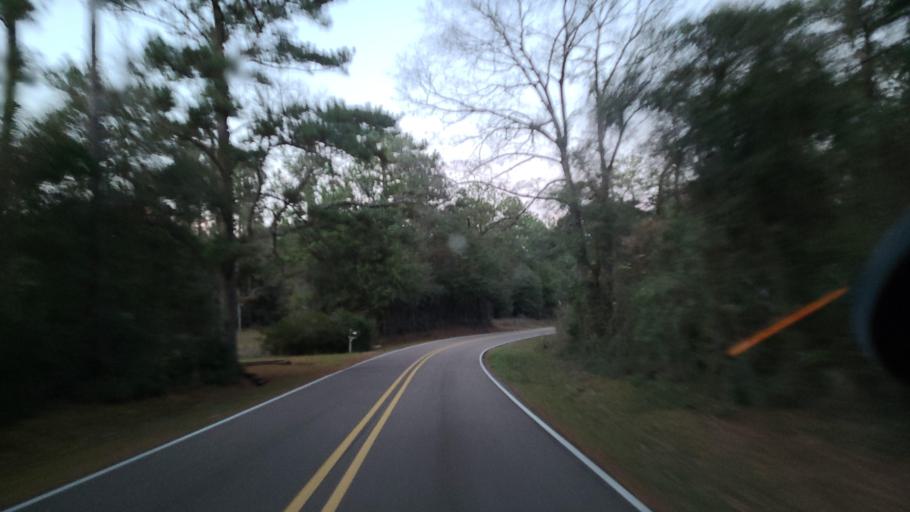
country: US
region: Mississippi
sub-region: Forrest County
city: Hattiesburg
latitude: 31.2398
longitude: -89.2421
